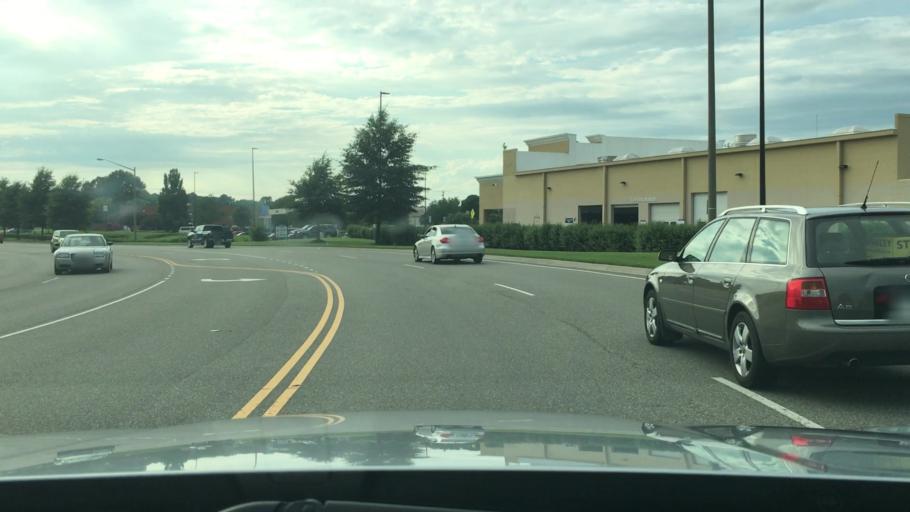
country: US
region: Virginia
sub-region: City of Petersburg
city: Petersburg
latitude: 37.2495
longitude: -77.3890
